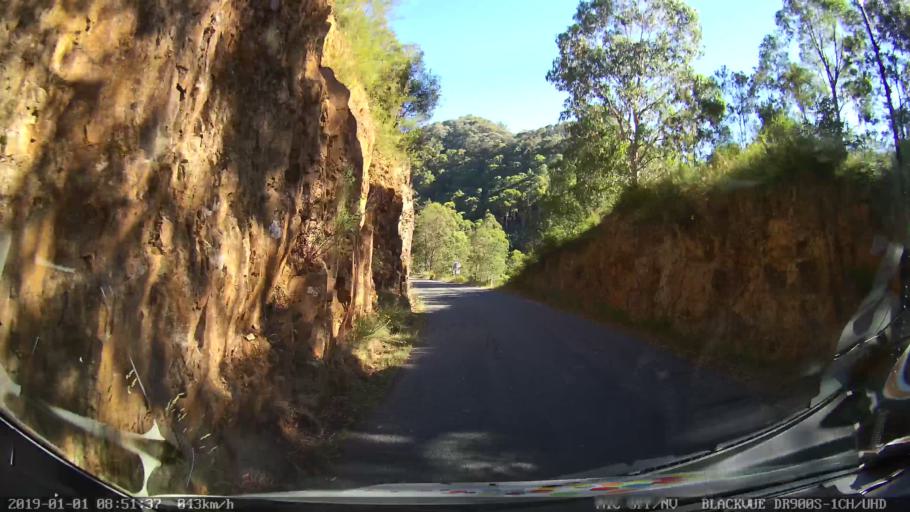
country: AU
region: New South Wales
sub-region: Snowy River
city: Jindabyne
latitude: -36.2704
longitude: 148.2017
